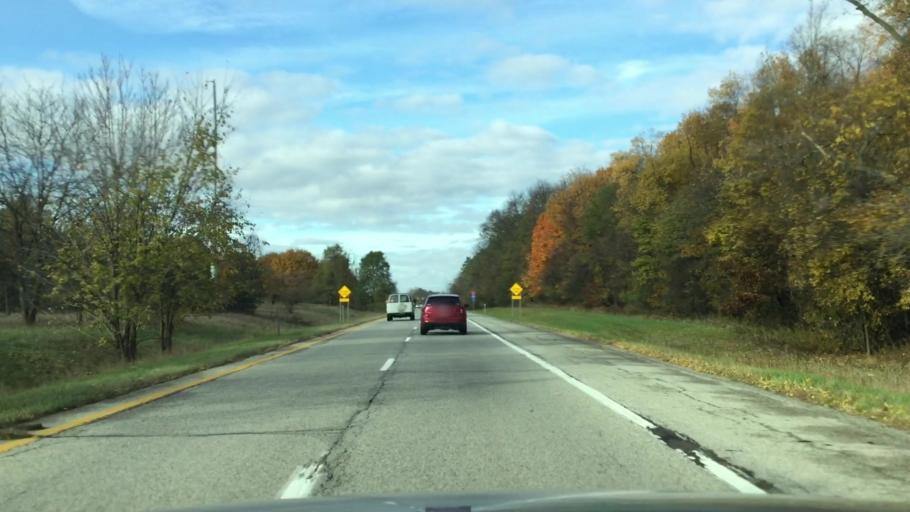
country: US
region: Michigan
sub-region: Kalamazoo County
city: Eastwood
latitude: 42.2695
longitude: -85.5142
